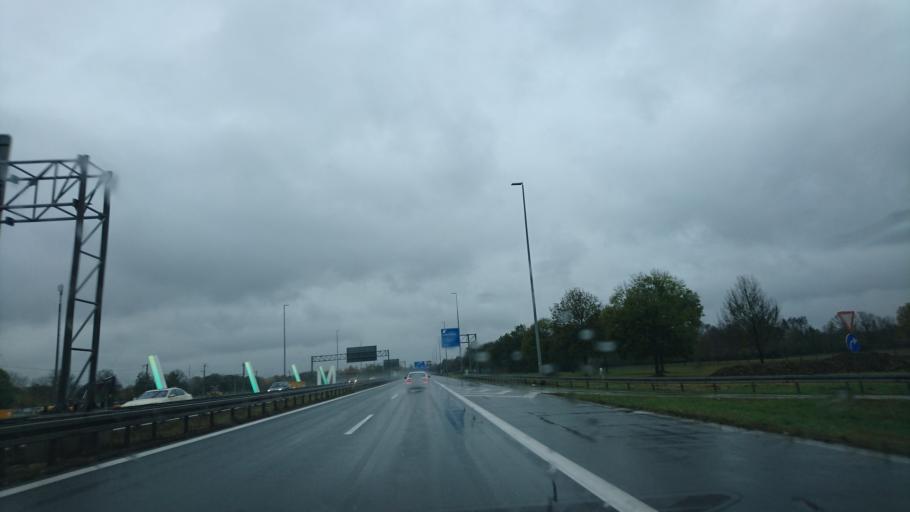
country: DE
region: Bavaria
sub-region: Upper Bavaria
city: Hallbergmoos
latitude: 48.3517
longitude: 11.7492
